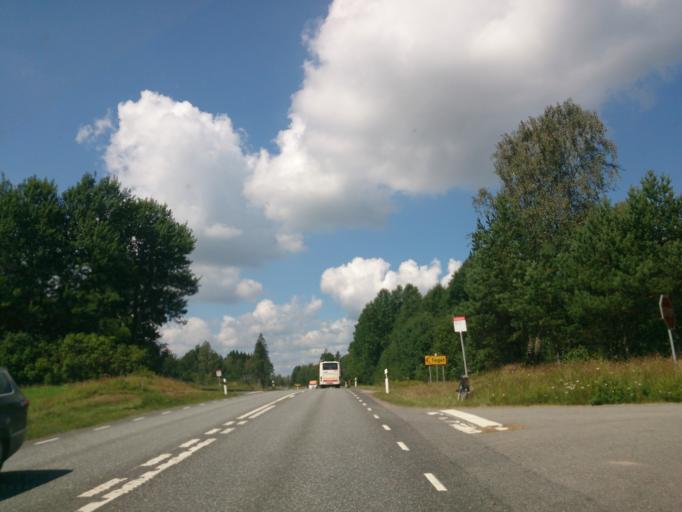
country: SE
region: Joenkoeping
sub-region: Gislaveds Kommun
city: Reftele
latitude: 57.1760
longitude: 13.6326
